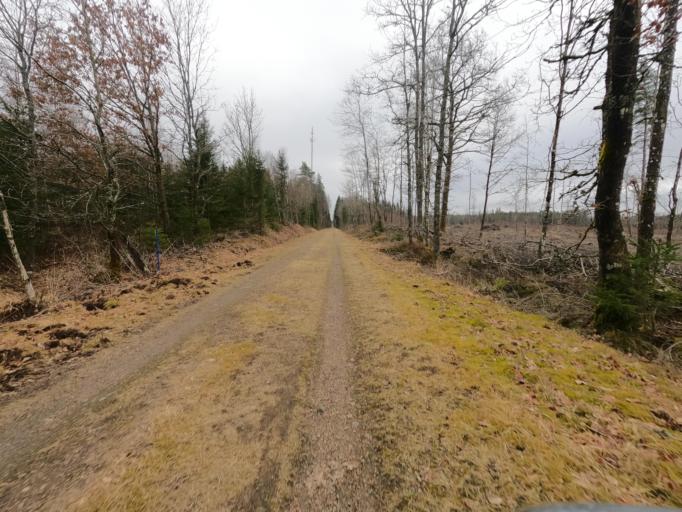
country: SE
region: Kronoberg
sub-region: Ljungby Kommun
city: Ljungby
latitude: 56.8234
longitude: 13.7305
